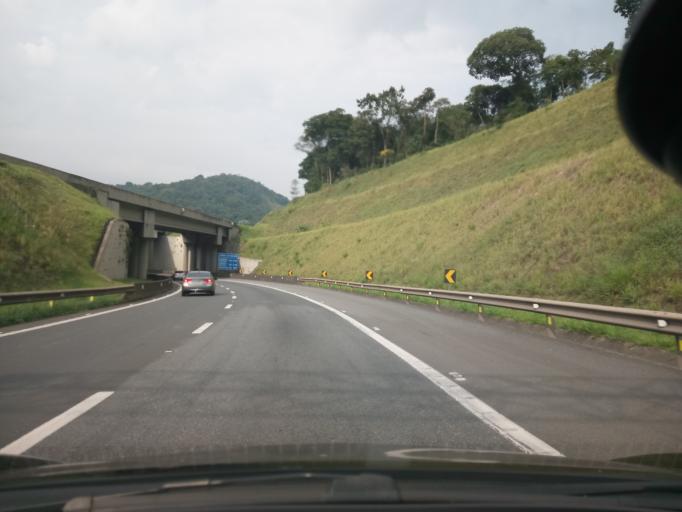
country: BR
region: Sao Paulo
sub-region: Sao Bernardo Do Campo
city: Sao Bernardo do Campo
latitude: -23.7634
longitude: -46.5485
